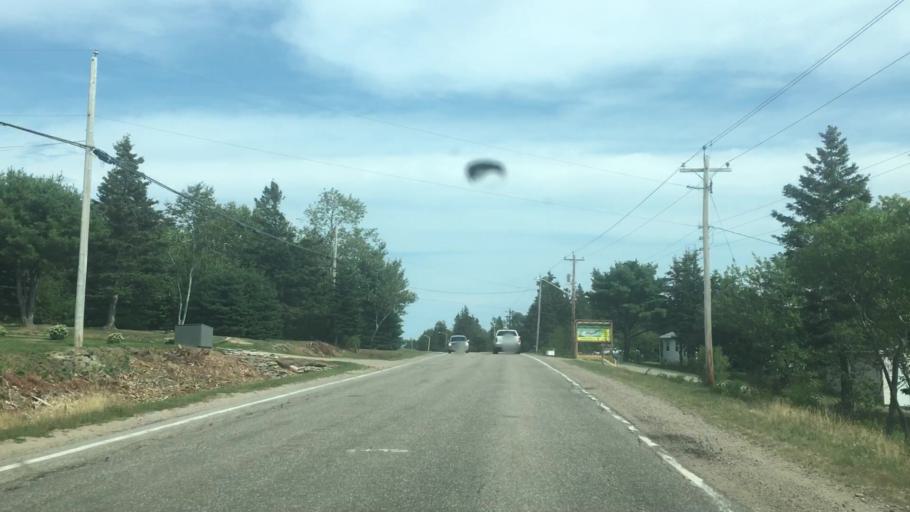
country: CA
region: Nova Scotia
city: Sydney Mines
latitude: 46.6897
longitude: -60.3906
